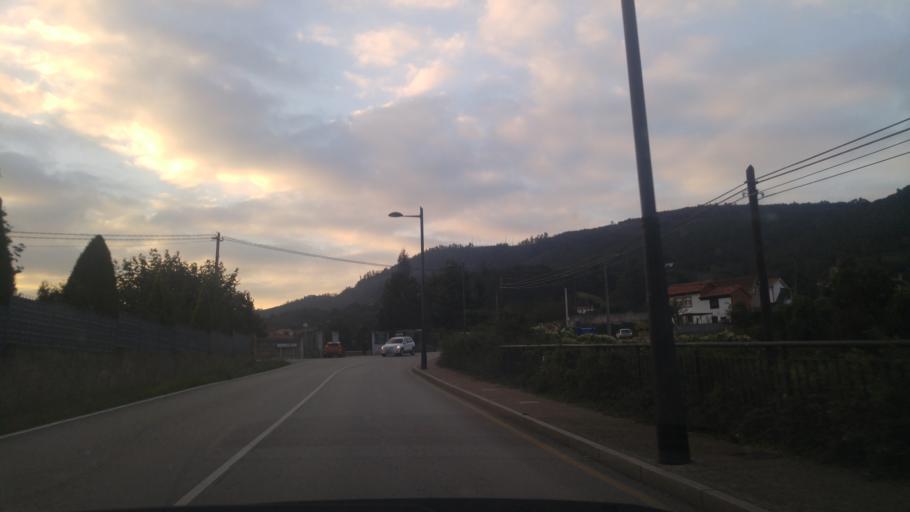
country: ES
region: Asturias
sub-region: Province of Asturias
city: Oviedo
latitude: 43.3745
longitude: -5.8637
